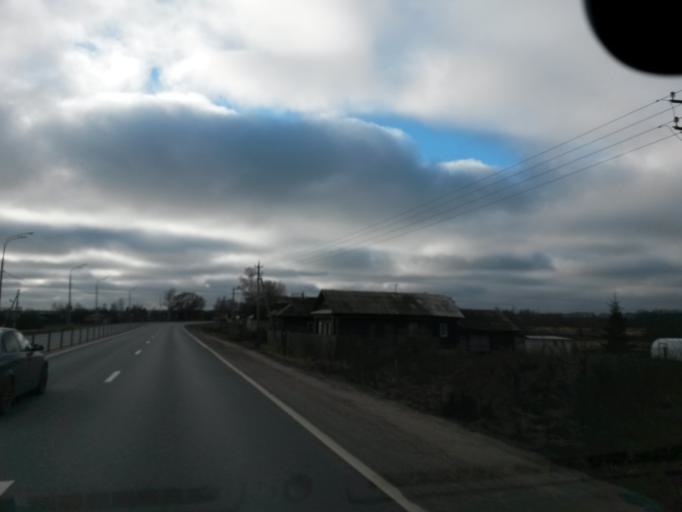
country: RU
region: Jaroslavl
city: Semibratovo
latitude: 57.3169
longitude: 39.5588
